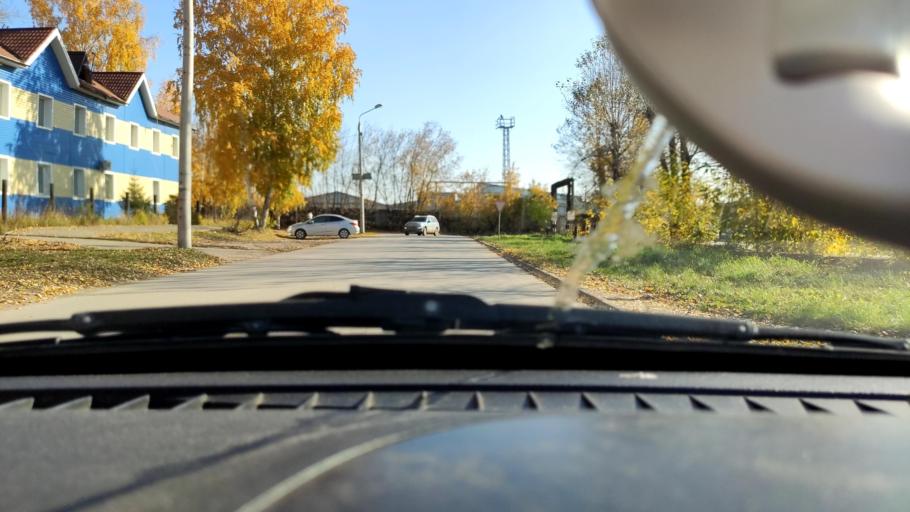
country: RU
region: Perm
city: Kondratovo
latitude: 58.0390
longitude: 56.1057
